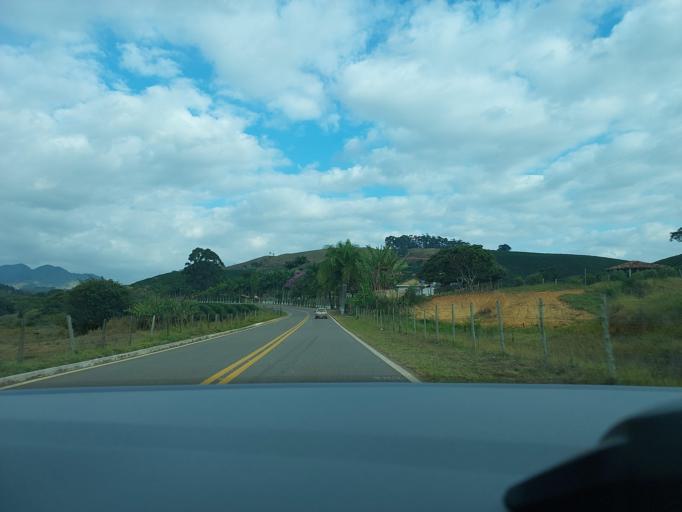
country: BR
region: Minas Gerais
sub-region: Visconde Do Rio Branco
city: Visconde do Rio Branco
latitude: -20.9267
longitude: -42.6358
